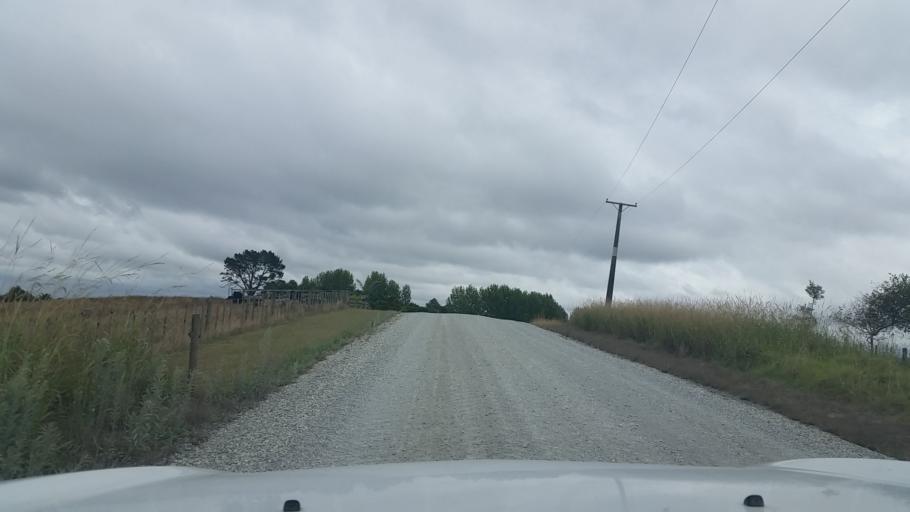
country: NZ
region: Northland
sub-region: Whangarei
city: Maungatapere
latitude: -35.6678
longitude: 174.1669
